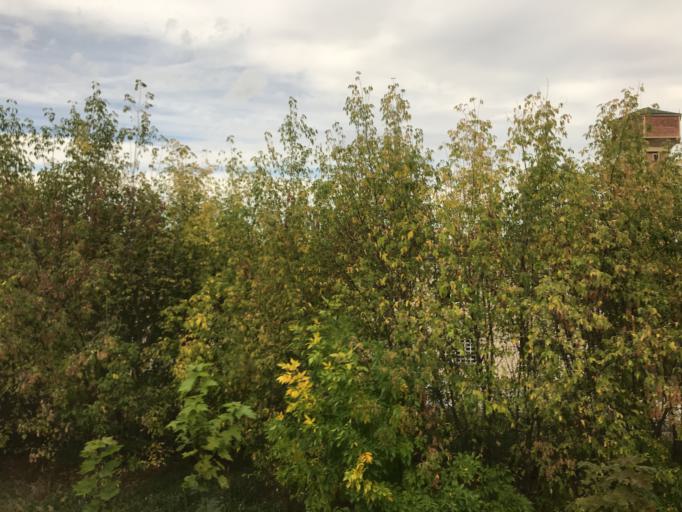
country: LT
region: Vilnius County
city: Naujamiestis
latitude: 54.6649
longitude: 25.2664
